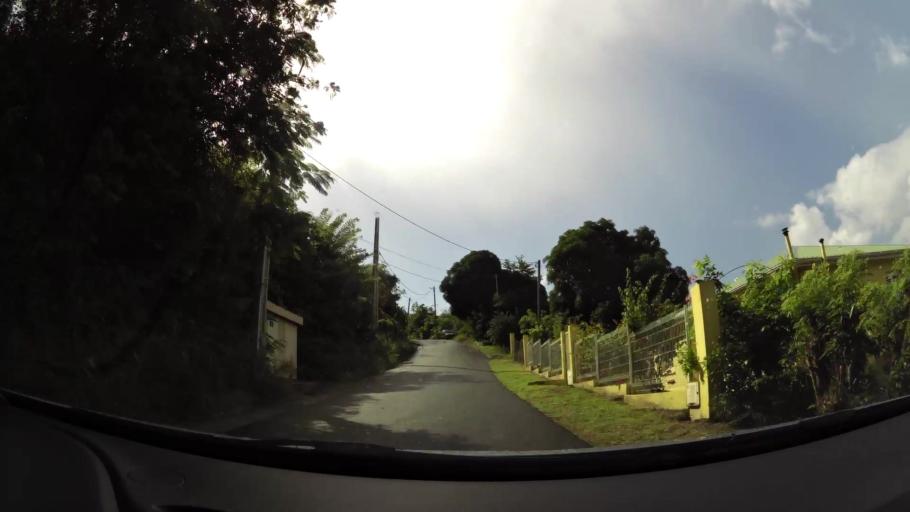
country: MQ
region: Martinique
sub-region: Martinique
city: Les Trois-Ilets
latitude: 14.4855
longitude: -61.0791
